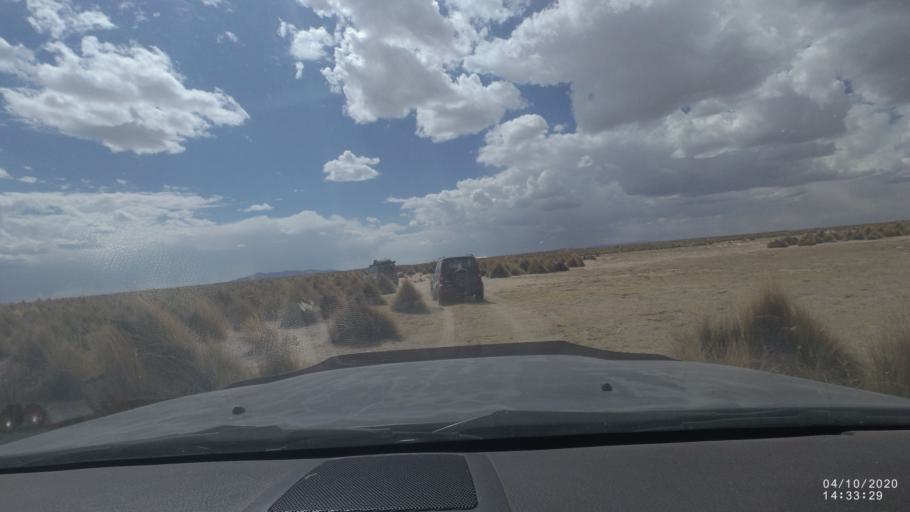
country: BO
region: Oruro
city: Poopo
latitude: -18.6713
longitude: -67.4671
